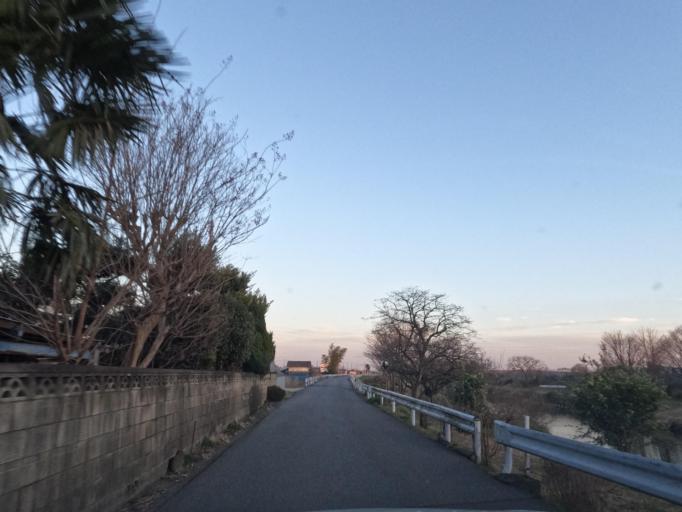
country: JP
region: Saitama
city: Kasukabe
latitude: 35.9287
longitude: 139.7457
